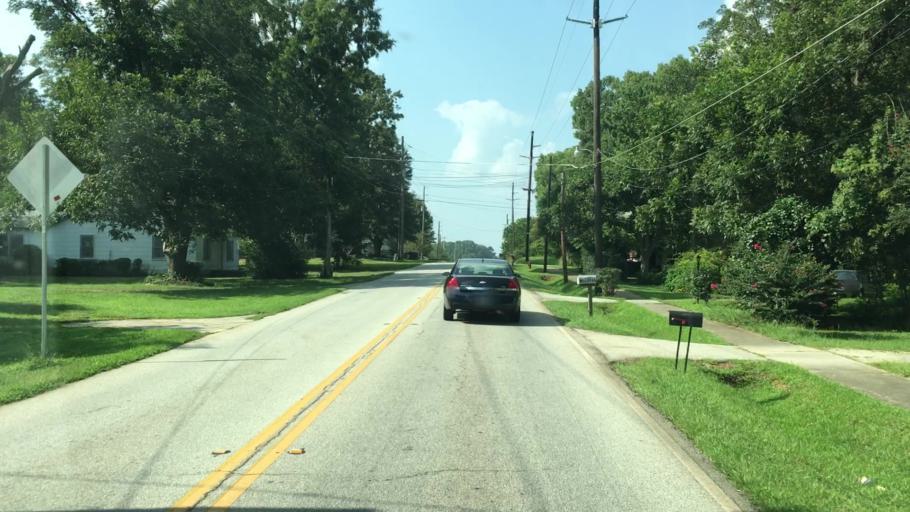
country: US
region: Georgia
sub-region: Walton County
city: Social Circle
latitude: 33.5232
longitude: -83.7369
